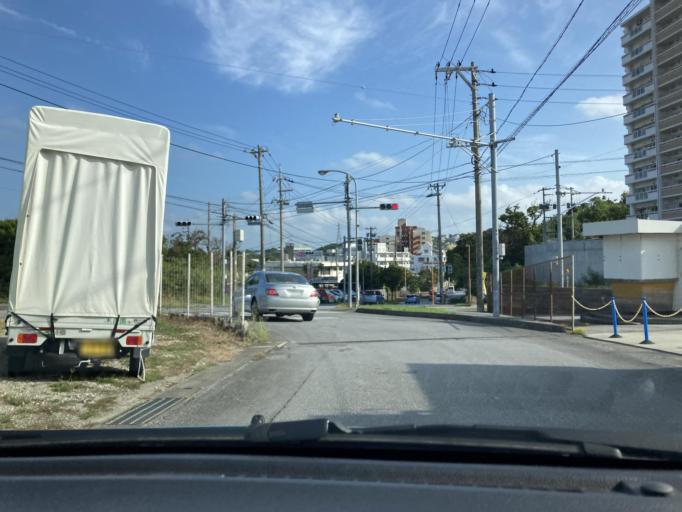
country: JP
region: Okinawa
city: Ginowan
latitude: 26.2351
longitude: 127.7453
